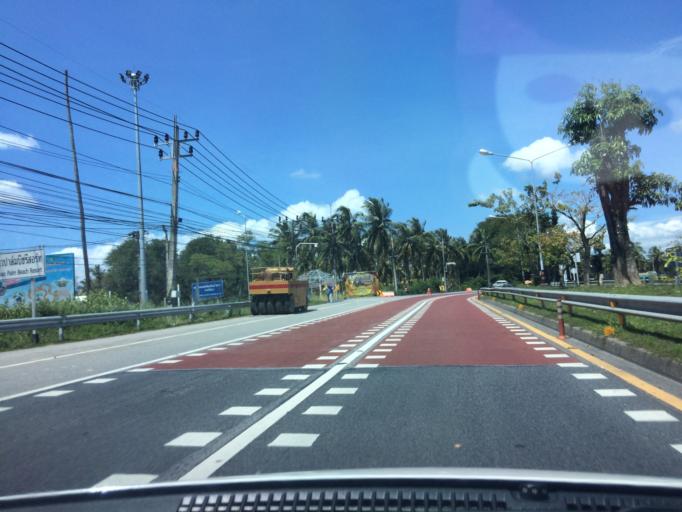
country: TH
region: Phuket
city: Thalang
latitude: 8.1585
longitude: 98.3050
